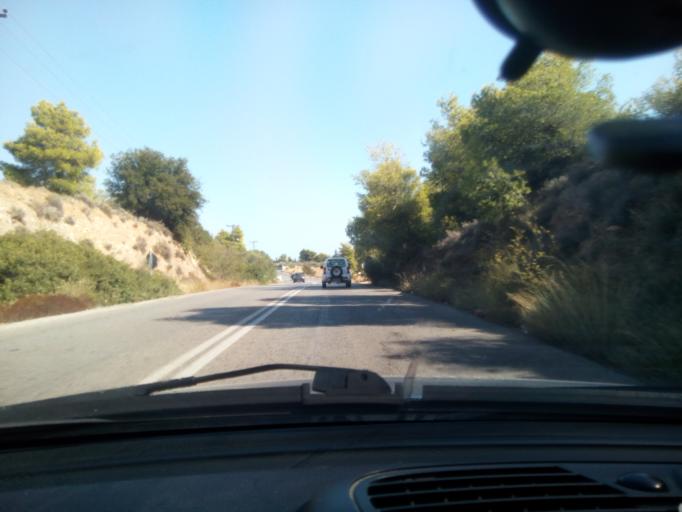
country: GR
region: Central Greece
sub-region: Nomos Evvoias
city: Malakonta
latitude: 38.4101
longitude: 23.7254
